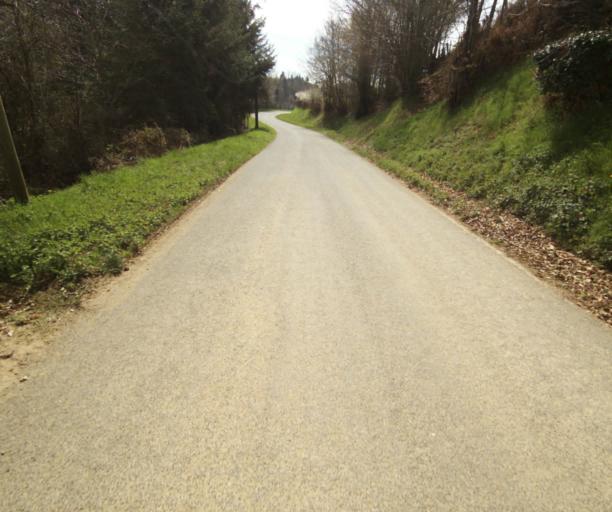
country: FR
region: Limousin
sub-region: Departement de la Correze
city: Naves
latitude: 45.3387
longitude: 1.7683
